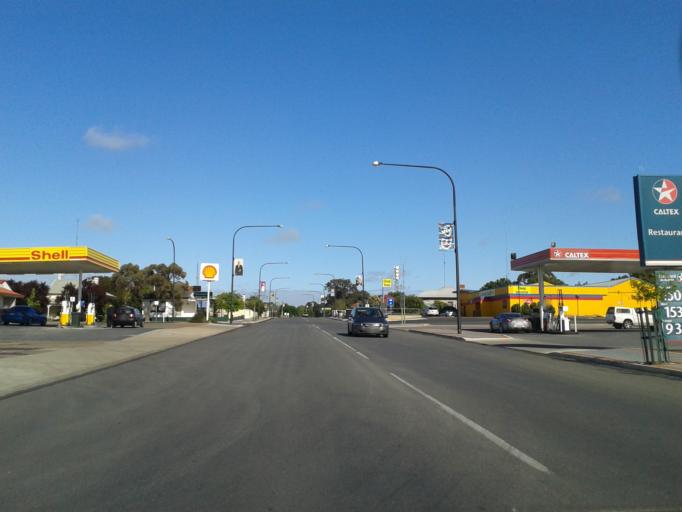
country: AU
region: South Australia
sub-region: Tatiara
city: Bordertown
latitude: -36.3082
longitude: 140.7730
